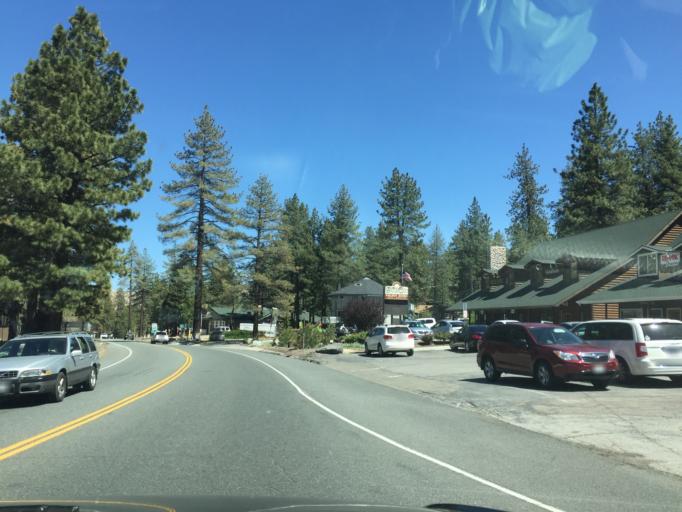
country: US
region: California
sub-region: San Bernardino County
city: Wrightwood
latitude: 34.3597
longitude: -117.6305
